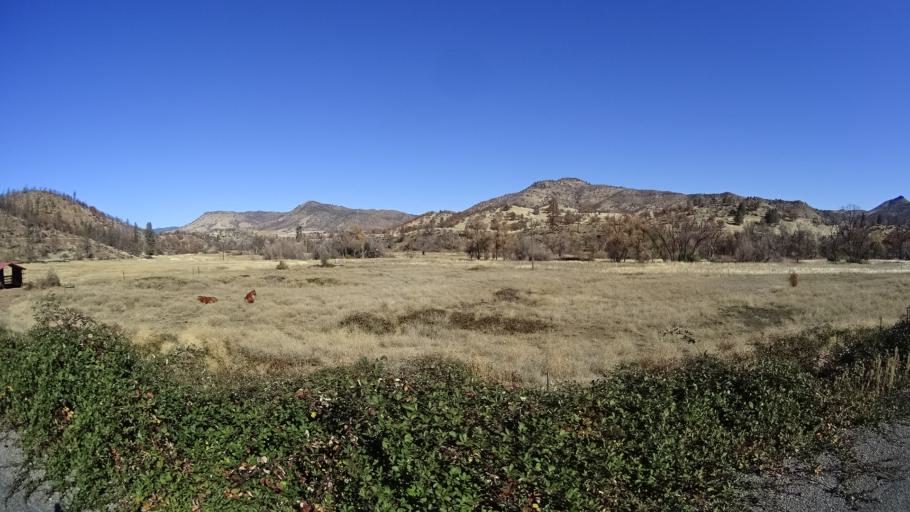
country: US
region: California
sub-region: Siskiyou County
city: Yreka
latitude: 41.9327
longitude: -122.5908
